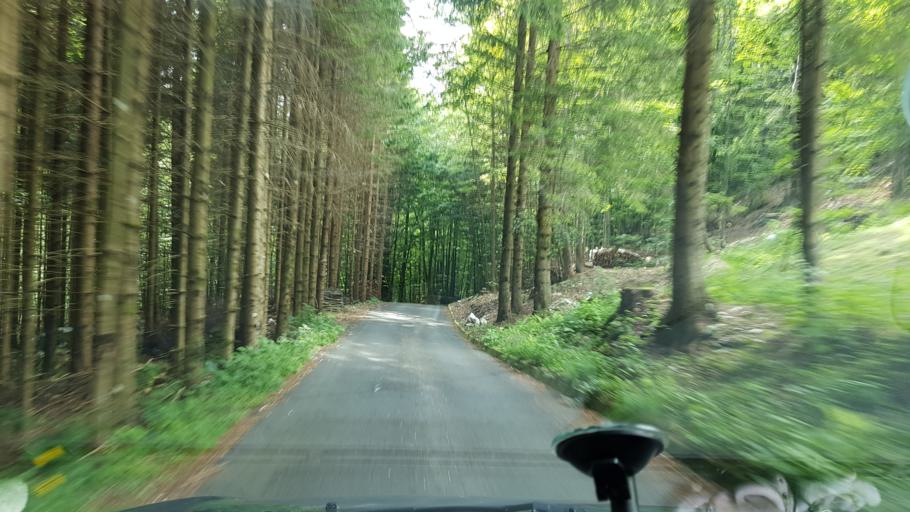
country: IT
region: Friuli Venezia Giulia
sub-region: Provincia di Udine
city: Taipana
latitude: 46.3348
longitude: 13.4152
